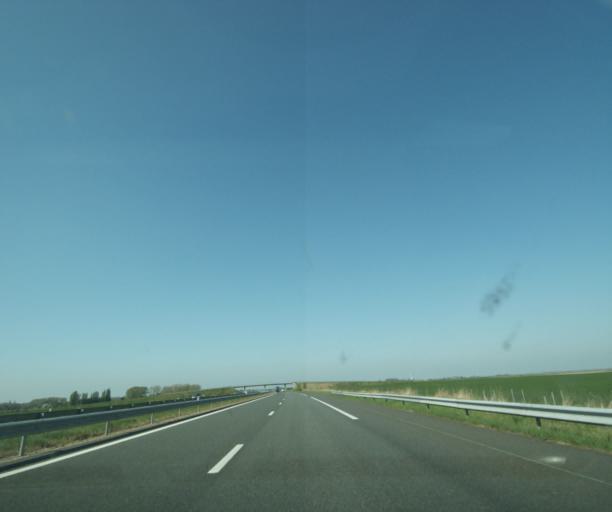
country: FR
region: Centre
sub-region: Departement du Loiret
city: Vimory
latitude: 47.9249
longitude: 2.6826
